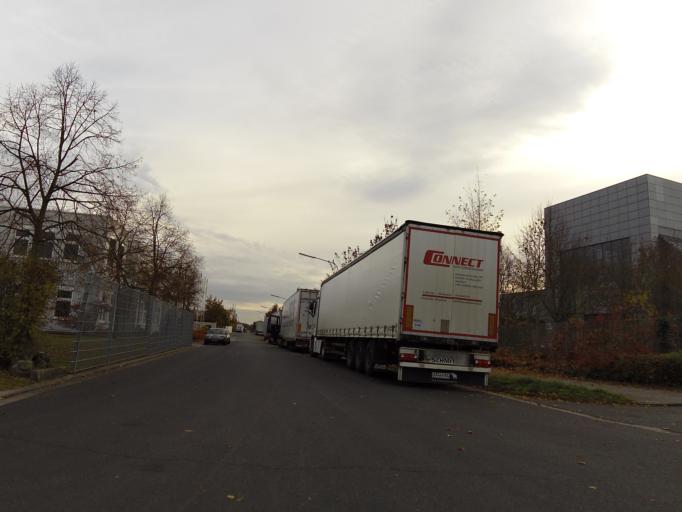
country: DE
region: Hesse
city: Morfelden-Walldorf
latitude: 49.9893
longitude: 8.5839
